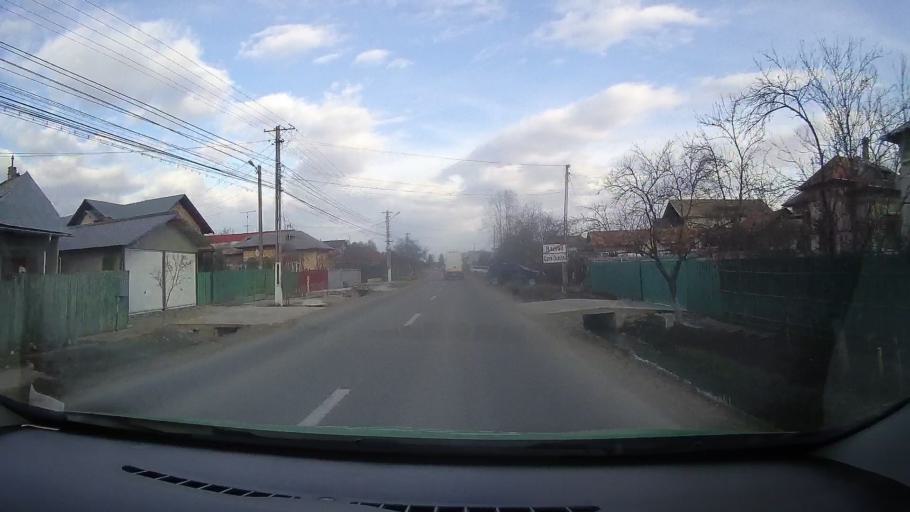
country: RO
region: Dambovita
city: Razvad
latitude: 44.9316
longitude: 25.5512
